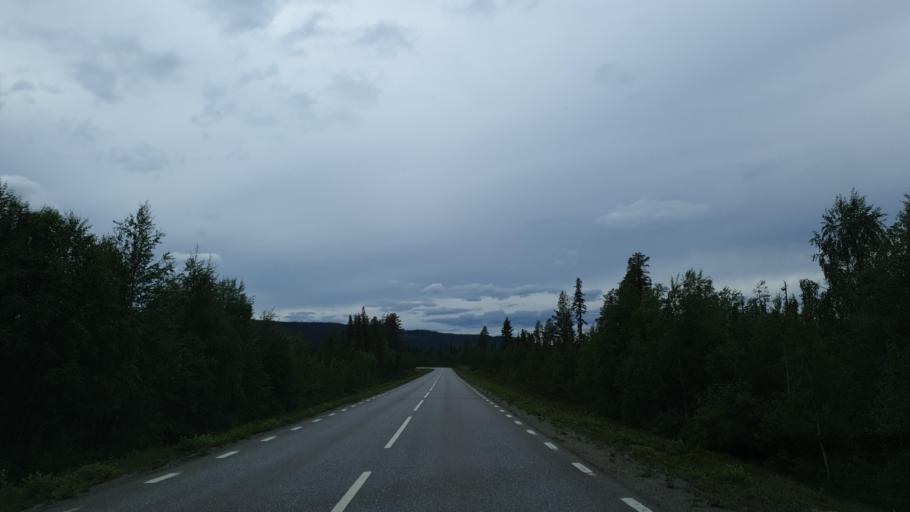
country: SE
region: Vaesterbotten
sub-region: Sorsele Kommun
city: Sorsele
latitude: 65.5446
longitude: 17.4321
